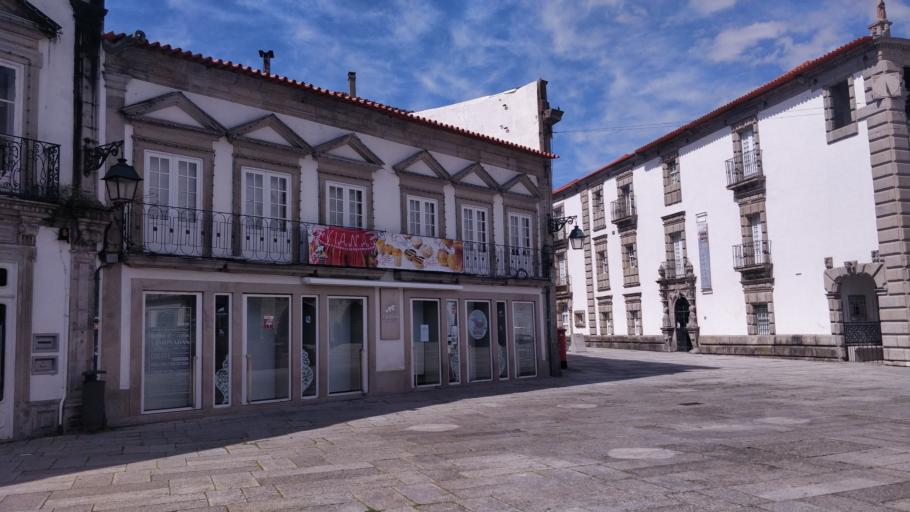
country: PT
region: Viana do Castelo
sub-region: Viana do Castelo
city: Viana do Castelo
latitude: 41.6935
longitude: -8.8283
